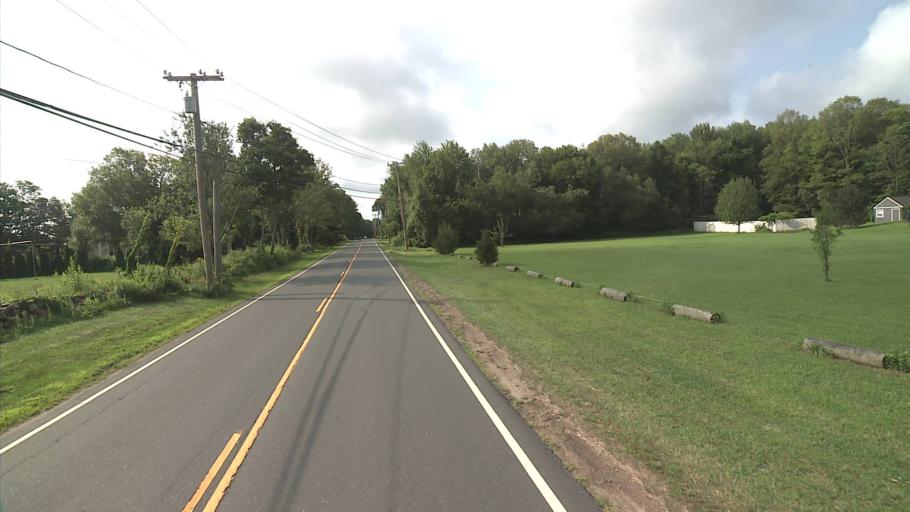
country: US
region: Connecticut
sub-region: Middlesex County
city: Moodus
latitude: 41.5402
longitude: -72.4119
